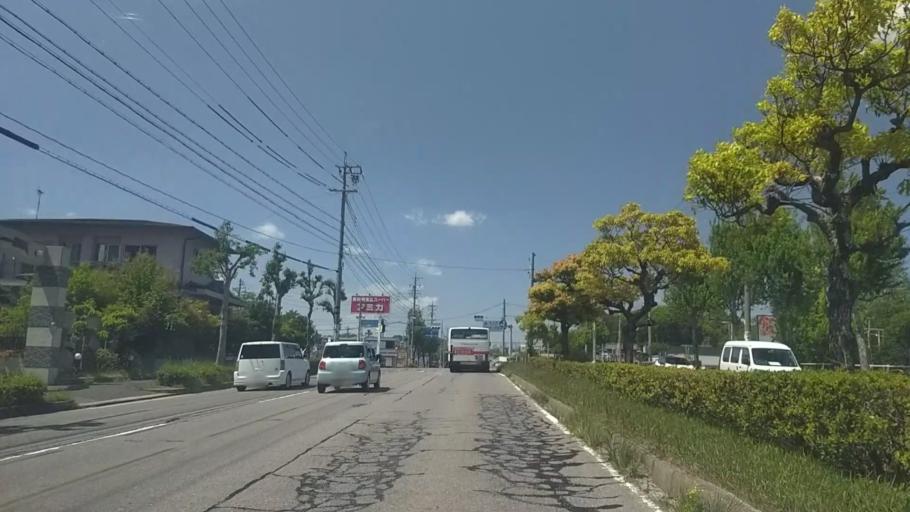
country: JP
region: Aichi
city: Okazaki
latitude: 34.9668
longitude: 137.1826
